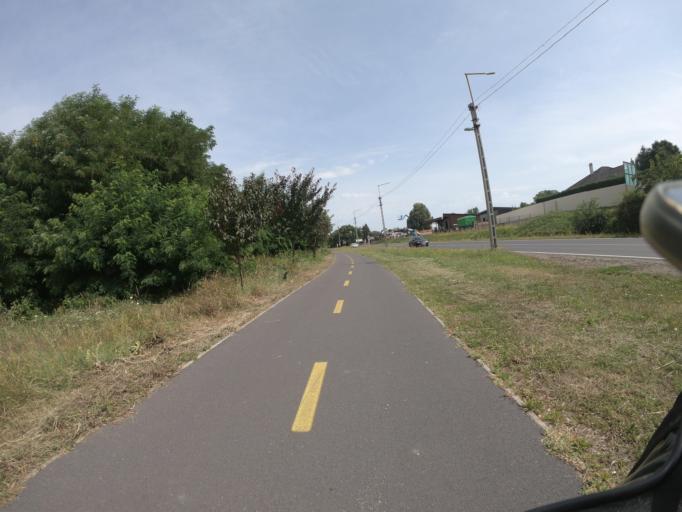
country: HU
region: Jasz-Nagykun-Szolnok
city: Tiszafured
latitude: 47.6252
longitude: 20.7480
